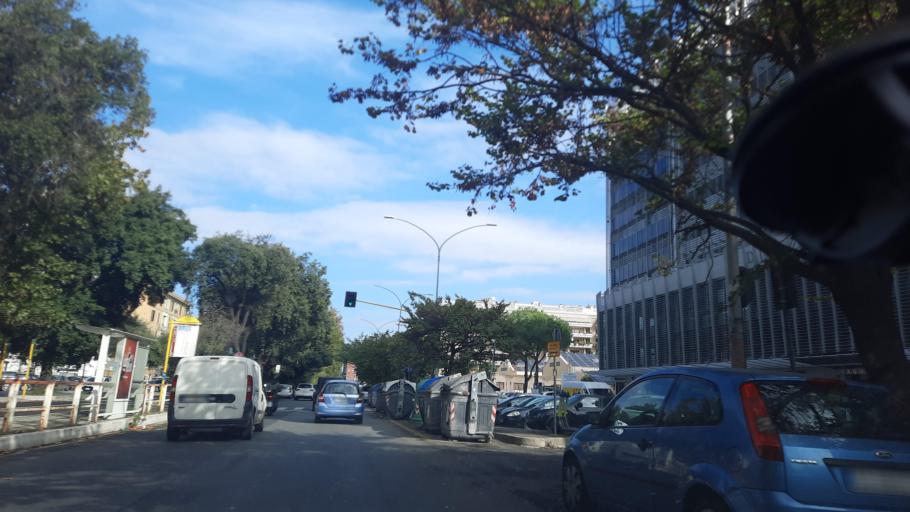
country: IT
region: Latium
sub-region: Citta metropolitana di Roma Capitale
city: Rome
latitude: 41.8653
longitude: 12.4792
